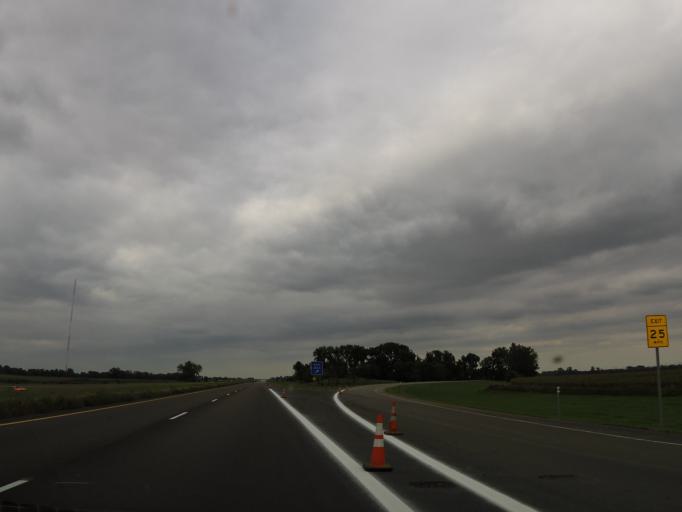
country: US
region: North Dakota
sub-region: Richland County
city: Wahpeton
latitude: 45.9741
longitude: -96.8359
